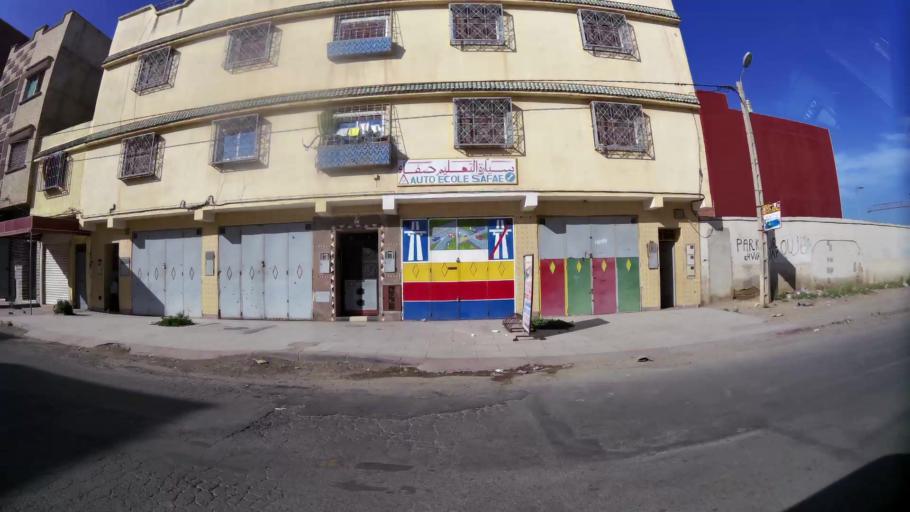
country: MA
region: Oriental
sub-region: Oujda-Angad
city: Oujda
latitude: 34.7093
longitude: -1.8913
